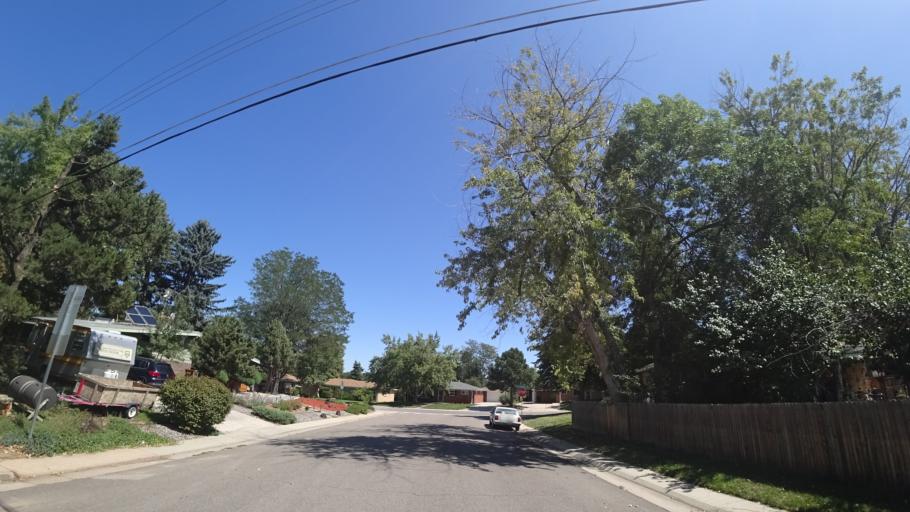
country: US
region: Colorado
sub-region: Arapahoe County
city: Littleton
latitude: 39.6090
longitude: -104.9897
